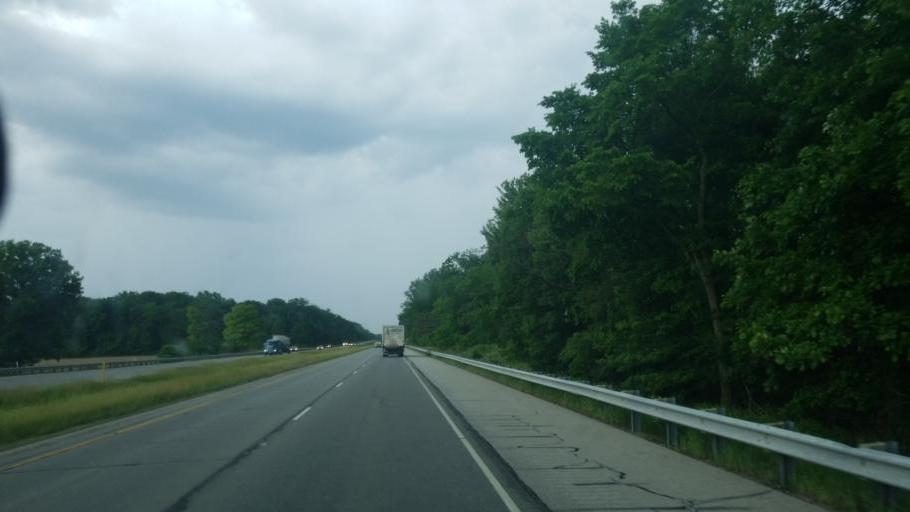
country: US
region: Indiana
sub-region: Whitley County
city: Churubusco
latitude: 41.1260
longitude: -85.3002
